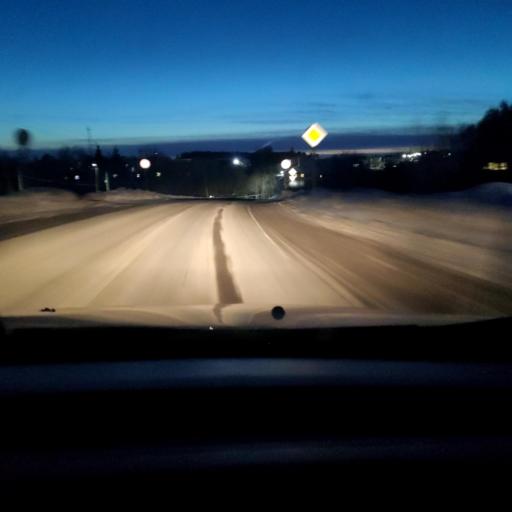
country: RU
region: Samara
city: Kinel'
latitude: 53.2684
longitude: 50.5919
